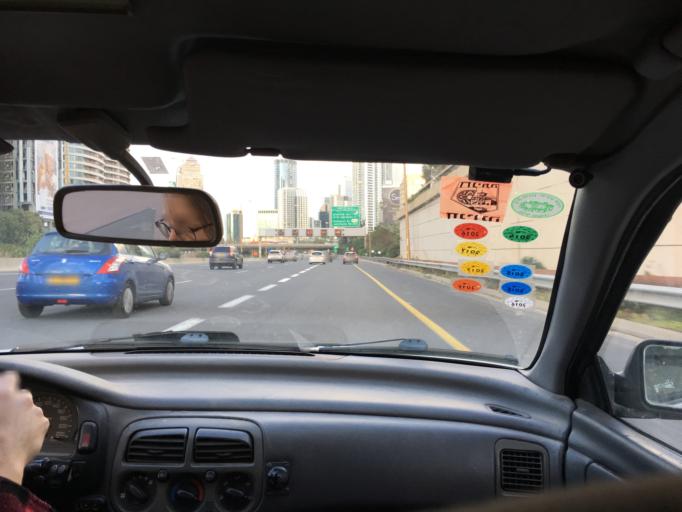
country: IL
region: Tel Aviv
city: Tel Aviv
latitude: 32.0773
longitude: 34.7953
